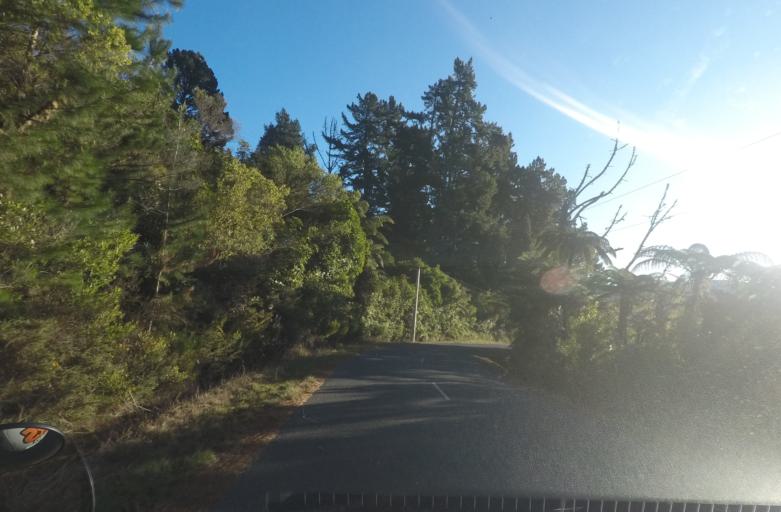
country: NZ
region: Marlborough
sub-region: Marlborough District
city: Picton
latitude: -41.2690
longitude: 173.9473
